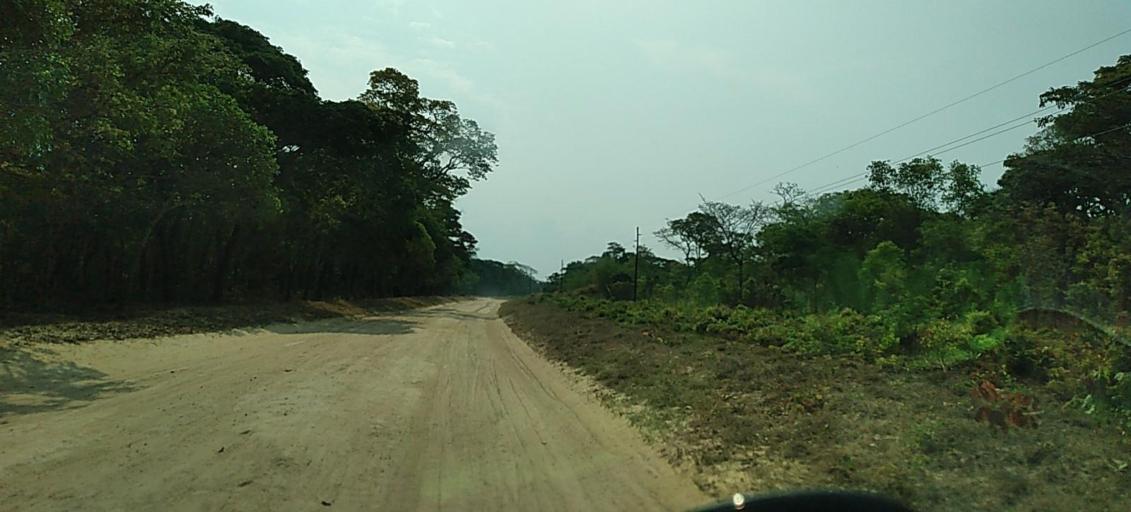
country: ZM
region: North-Western
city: Solwezi
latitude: -12.6811
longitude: 26.3822
